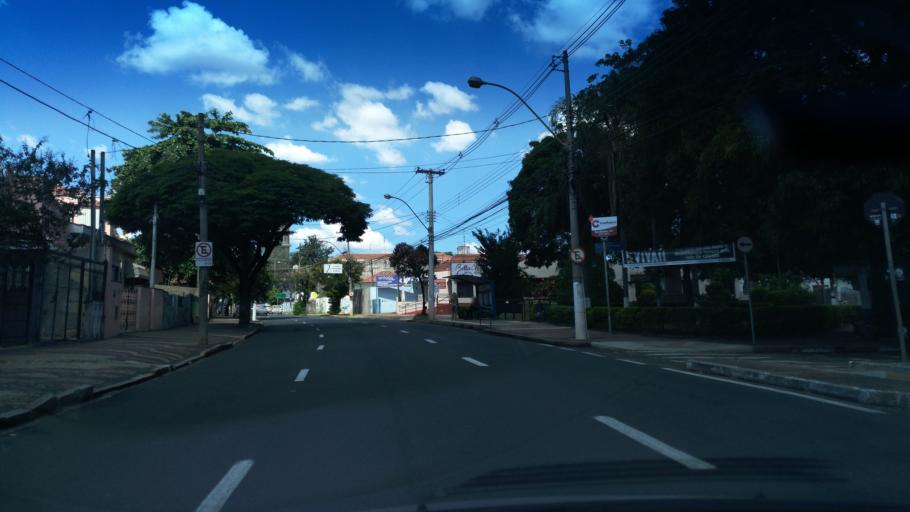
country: BR
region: Sao Paulo
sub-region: Campinas
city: Campinas
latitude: -22.9190
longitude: -47.0542
